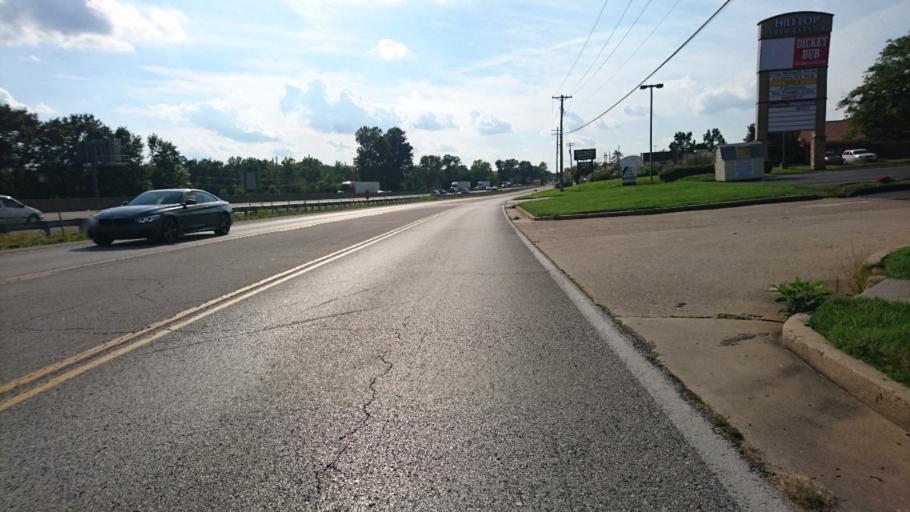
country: US
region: Missouri
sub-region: Saint Louis County
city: Eureka
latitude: 38.5044
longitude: -90.6419
